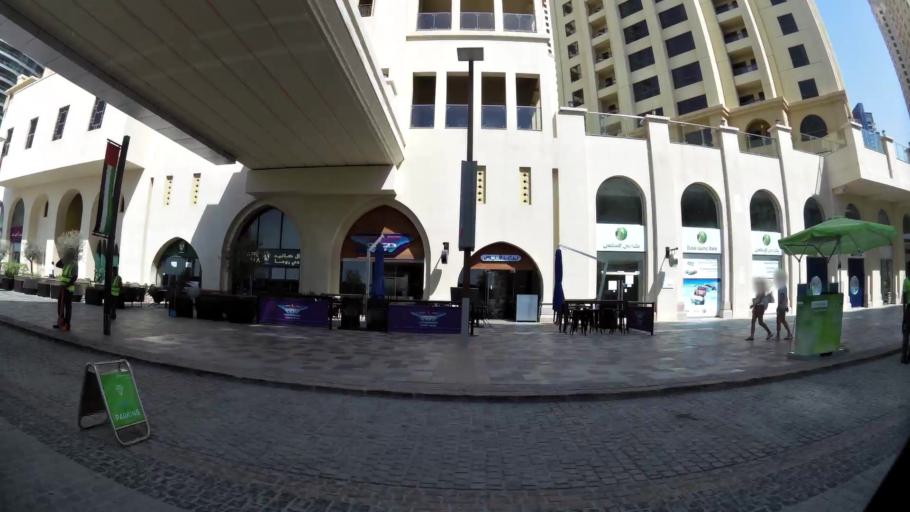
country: AE
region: Dubai
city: Dubai
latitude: 25.0788
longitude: 55.1349
